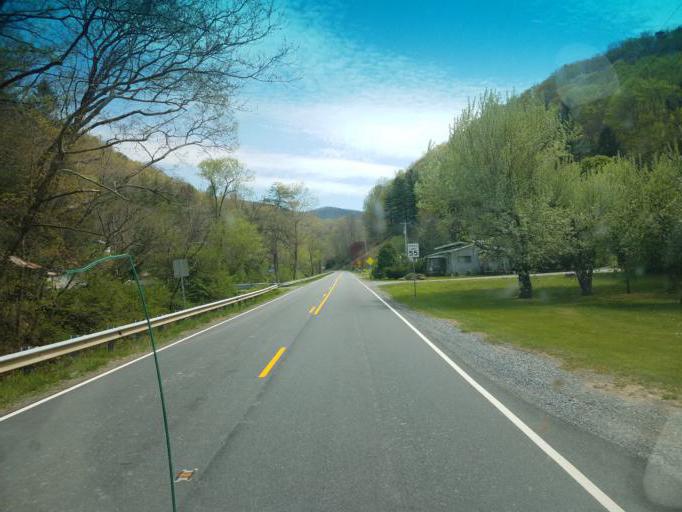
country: US
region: Virginia
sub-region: Smyth County
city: Marion
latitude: 36.8148
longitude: -81.4669
